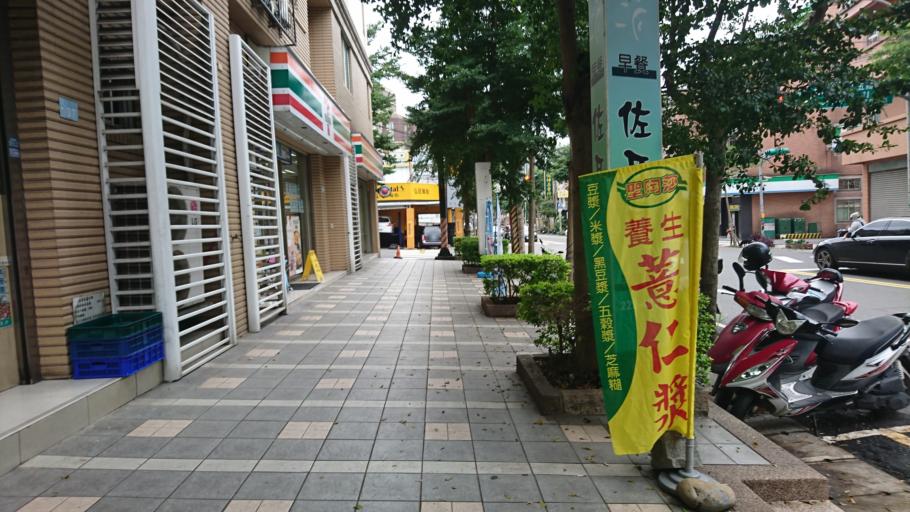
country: TW
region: Taiwan
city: Taoyuan City
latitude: 25.0583
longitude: 121.2953
